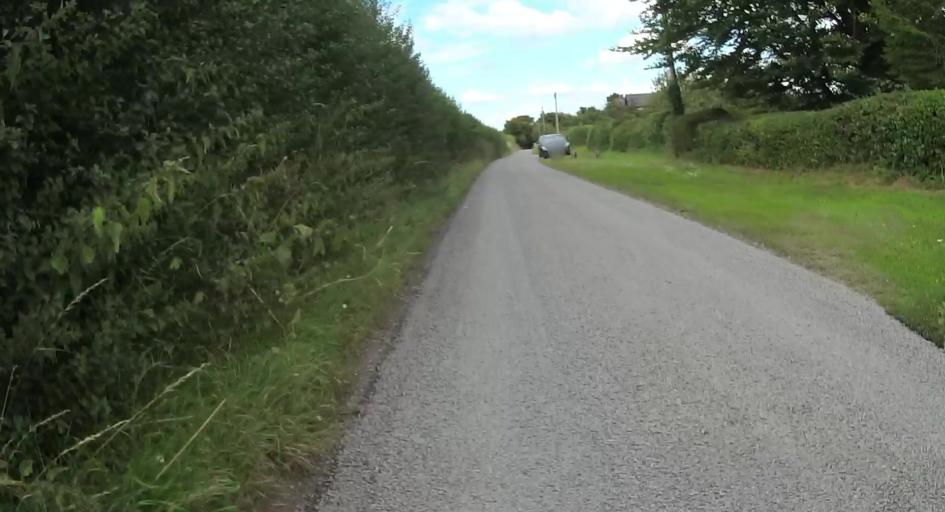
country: GB
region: England
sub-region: Hampshire
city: Kings Worthy
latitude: 51.1432
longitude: -1.3323
